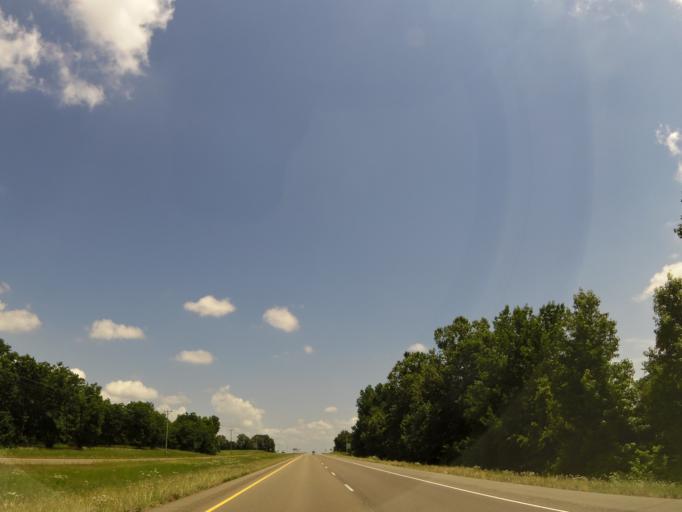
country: US
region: Tennessee
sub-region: Lauderdale County
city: Halls
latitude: 35.8952
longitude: -89.2417
